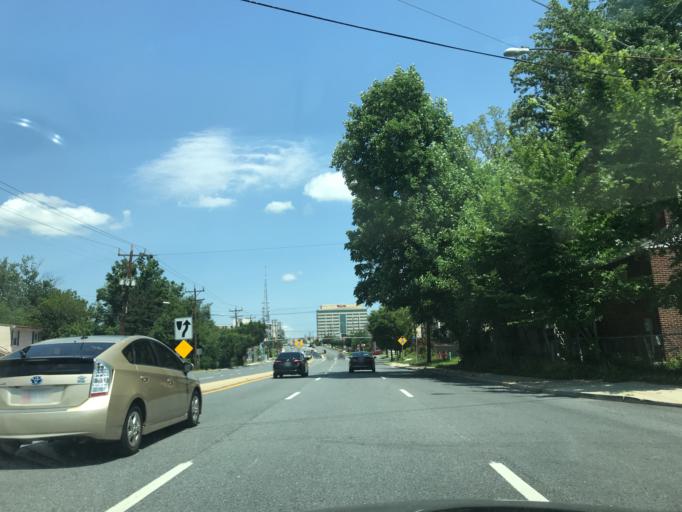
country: US
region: Maryland
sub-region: Montgomery County
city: Wheaton
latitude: 39.0368
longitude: -77.0615
